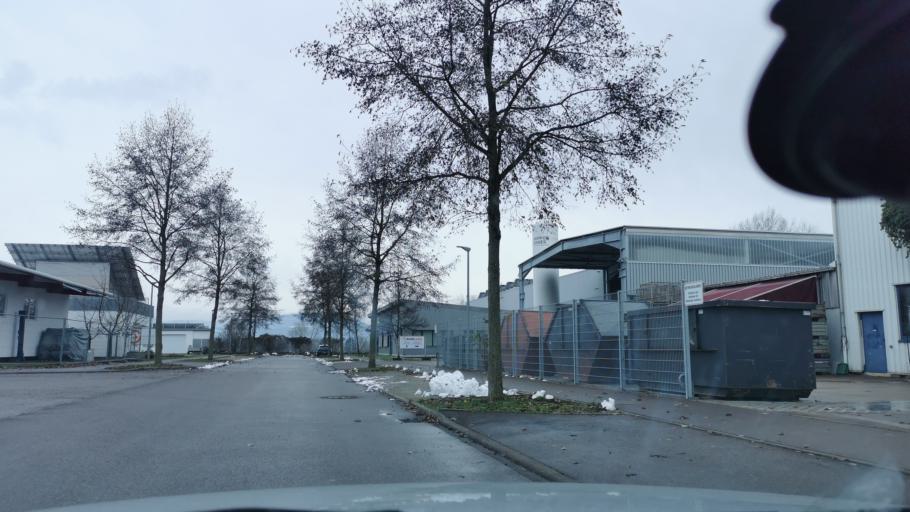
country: DE
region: Baden-Wuerttemberg
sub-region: Regierungsbezirk Stuttgart
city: Eislingen
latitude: 48.7107
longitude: 9.6887
